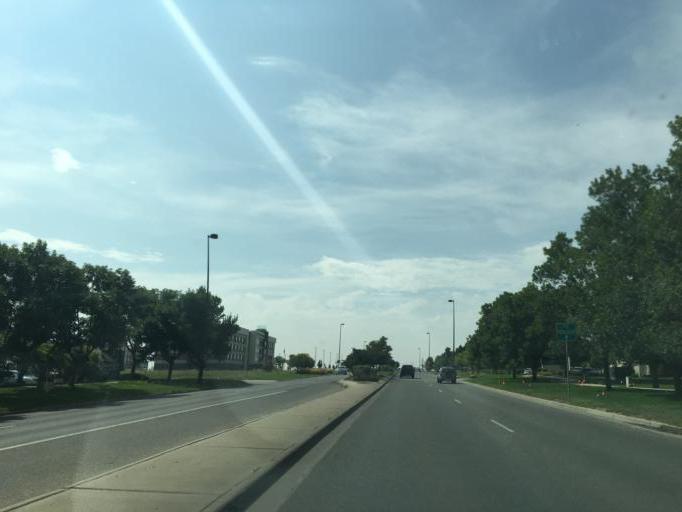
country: US
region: Colorado
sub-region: Adams County
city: Aurora
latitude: 39.8218
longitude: -104.7720
